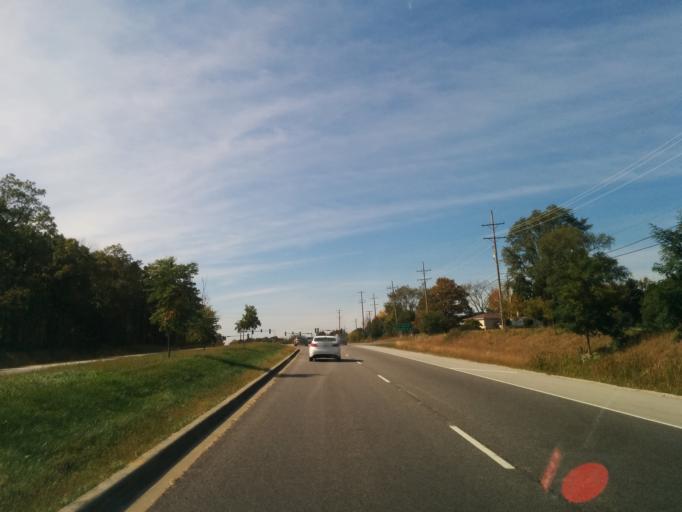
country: US
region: Illinois
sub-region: DuPage County
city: Warrenville
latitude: 41.8313
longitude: -88.1440
